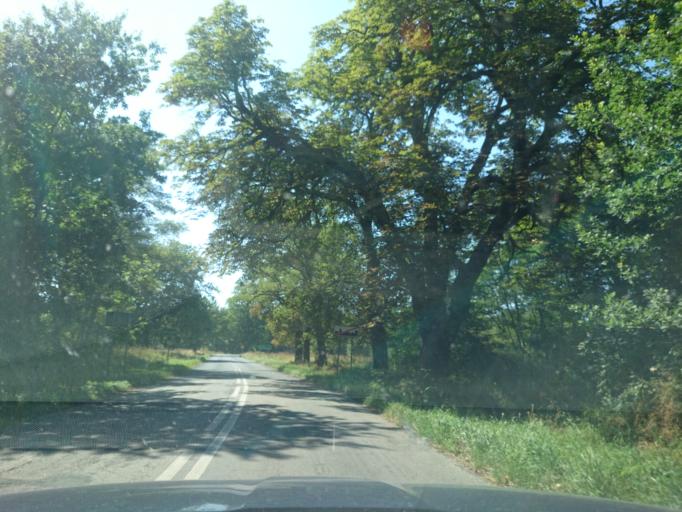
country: PL
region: West Pomeranian Voivodeship
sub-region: Powiat policki
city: Nowe Warpno
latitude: 53.6754
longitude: 14.3731
